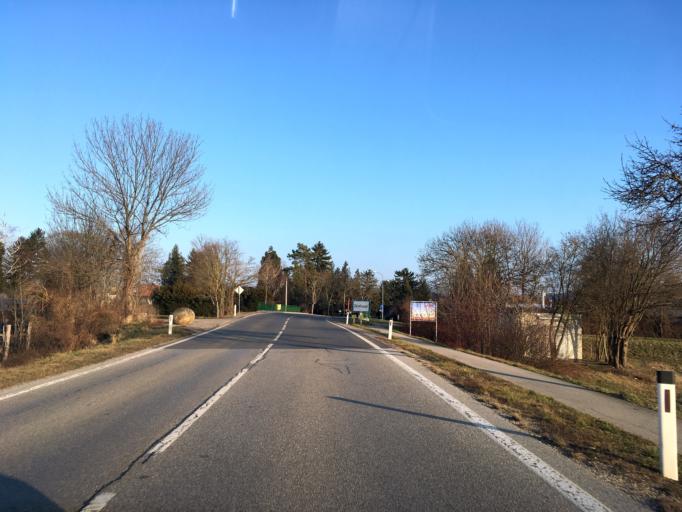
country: AT
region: Lower Austria
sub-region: Politischer Bezirk Tulln
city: Konigstetten
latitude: 48.3293
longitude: 16.1704
